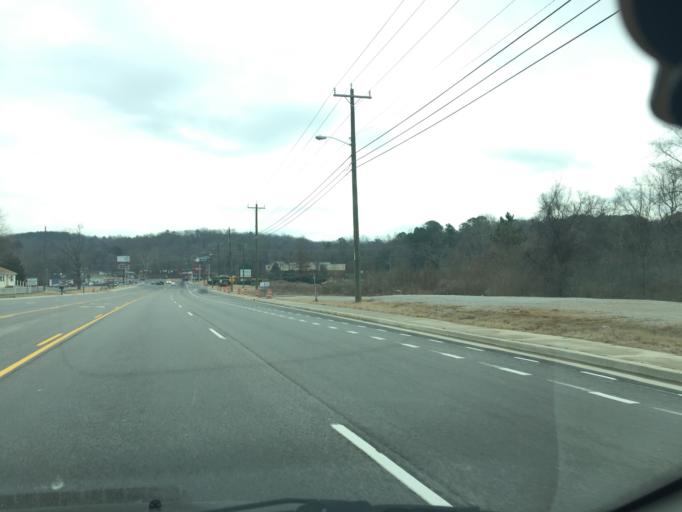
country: US
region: Tennessee
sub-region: Hamilton County
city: East Brainerd
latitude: 35.0014
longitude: -85.1360
